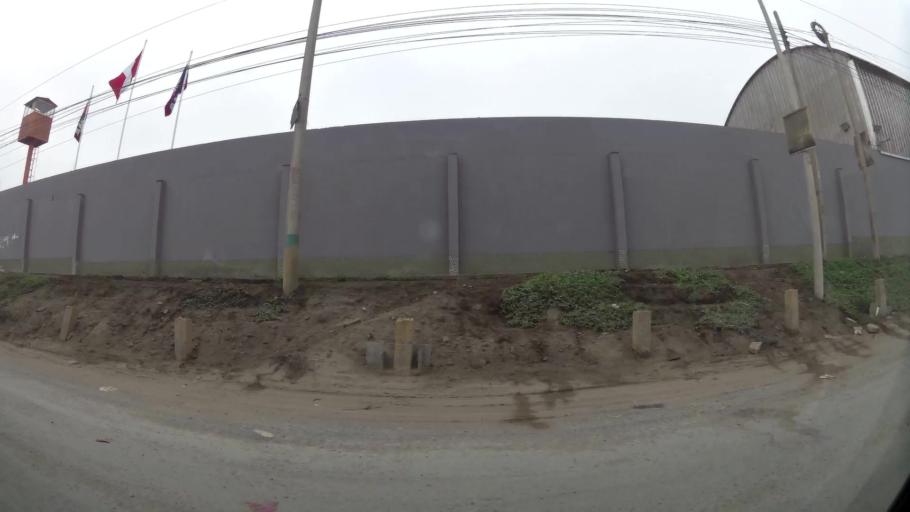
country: PE
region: Lima
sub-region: Lima
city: Surco
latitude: -12.2179
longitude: -76.9759
